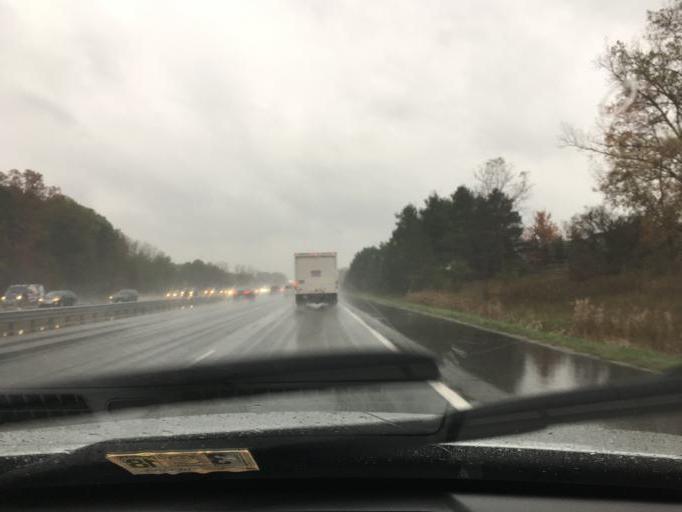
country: US
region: Michigan
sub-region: Oakland County
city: Waterford
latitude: 42.7166
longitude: -83.3436
